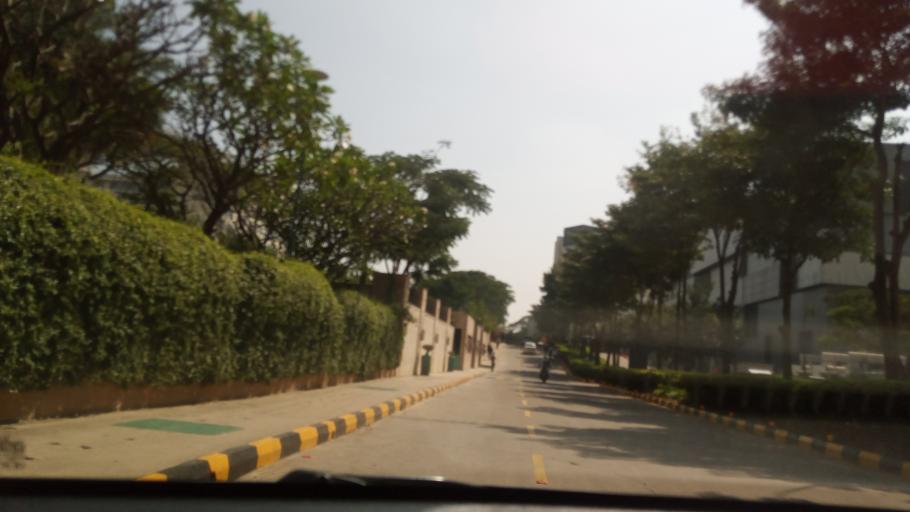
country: IN
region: Karnataka
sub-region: Bangalore Rural
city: Hoskote
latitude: 12.9908
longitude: 77.7291
